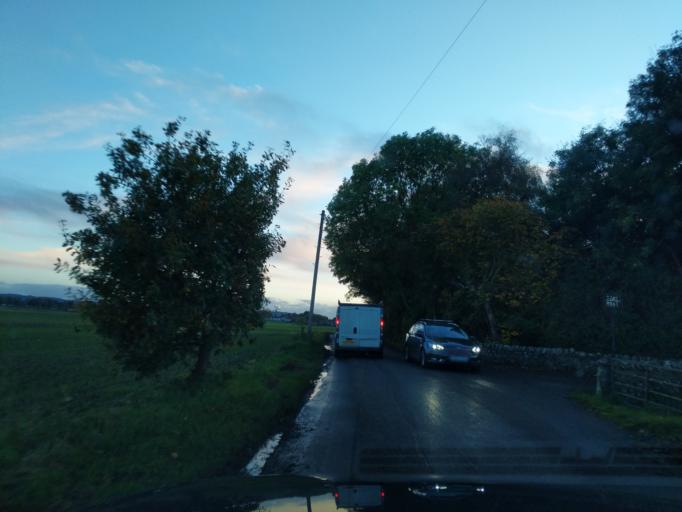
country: GB
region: Scotland
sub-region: Fife
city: Leuchars
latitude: 56.3939
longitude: -2.8702
